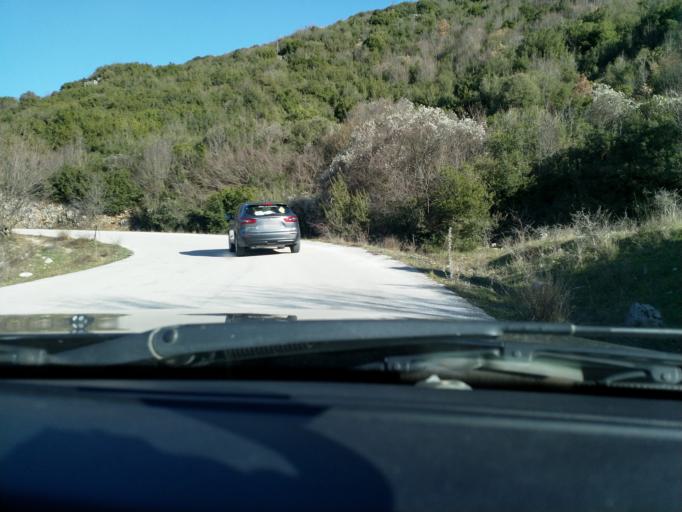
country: GR
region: Epirus
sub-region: Nomos Ioanninon
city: Kalpaki
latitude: 39.9024
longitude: 20.6723
